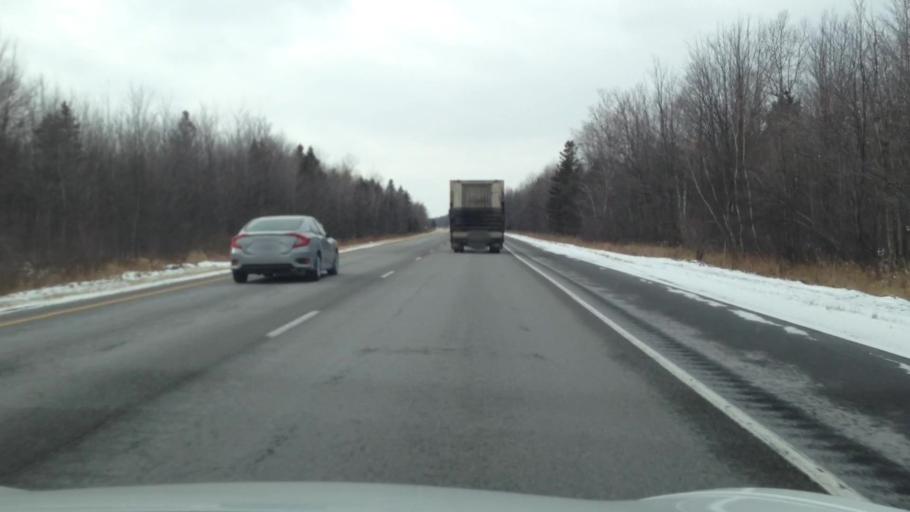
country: CA
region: Ontario
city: Casselman
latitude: 45.3159
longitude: -75.1862
